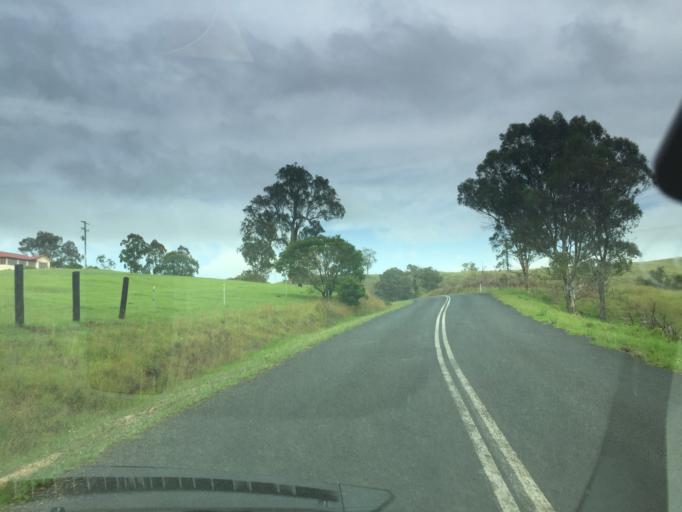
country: AU
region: New South Wales
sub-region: Bega Valley
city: Bega
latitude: -36.7578
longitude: 149.6830
